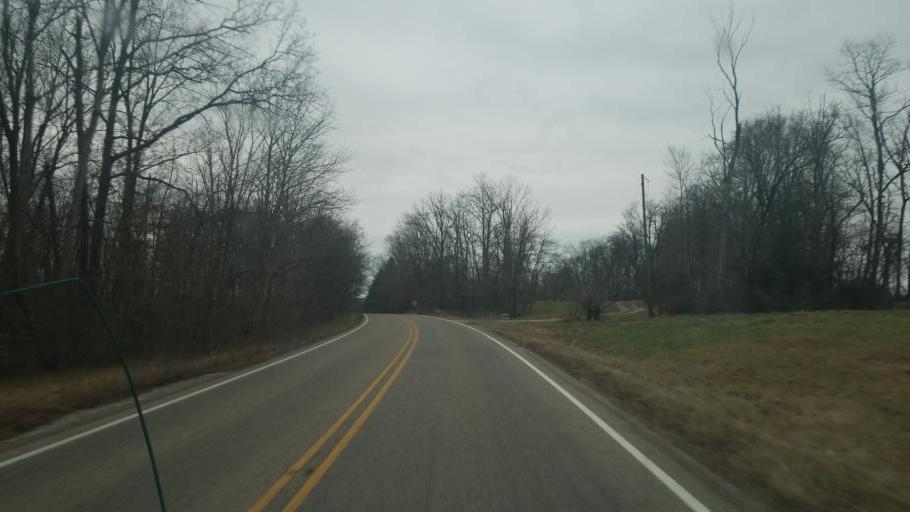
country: US
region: Indiana
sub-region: Owen County
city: Spencer
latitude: 39.3564
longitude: -86.9382
